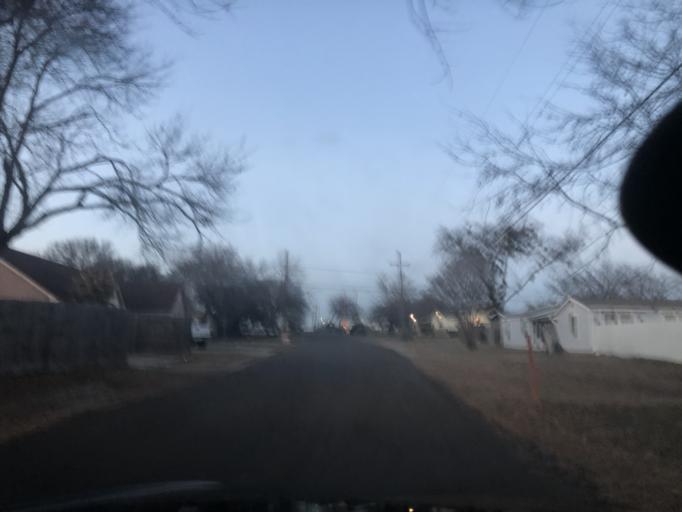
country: US
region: Texas
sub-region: Tarrant County
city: White Settlement
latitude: 32.7272
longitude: -97.4914
